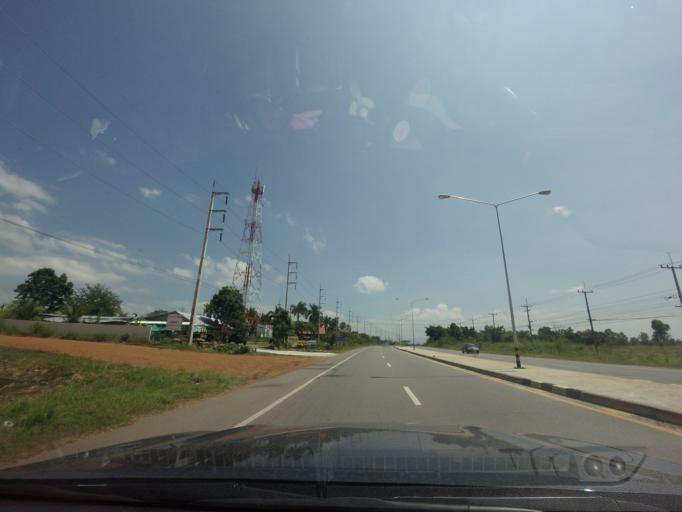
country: TH
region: Phetchabun
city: Lom Sak
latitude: 16.7680
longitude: 101.1804
